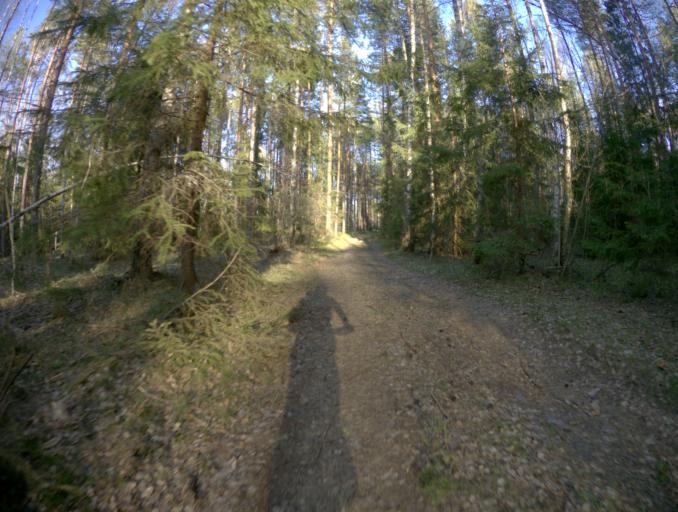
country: RU
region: Vladimir
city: Mezinovskiy
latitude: 55.6120
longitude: 40.3881
